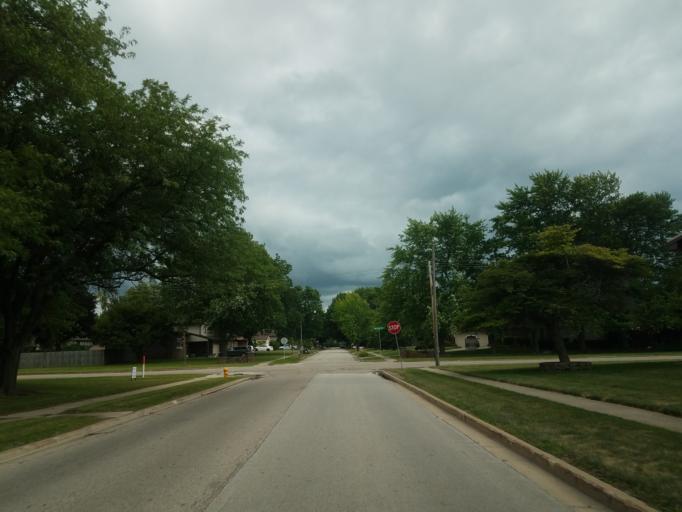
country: US
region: Illinois
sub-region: McLean County
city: Bloomington
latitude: 40.4803
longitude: -88.9463
